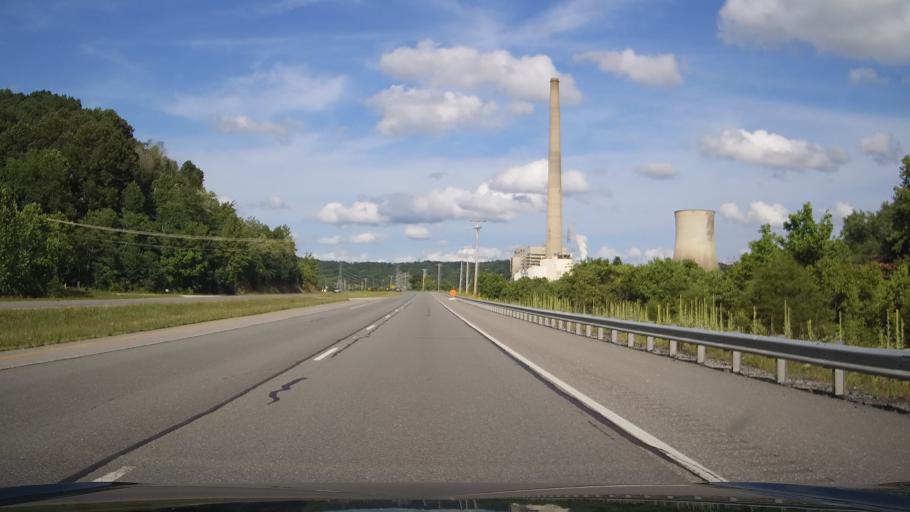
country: US
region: Kentucky
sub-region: Lawrence County
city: Louisa
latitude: 38.1716
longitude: -82.6283
